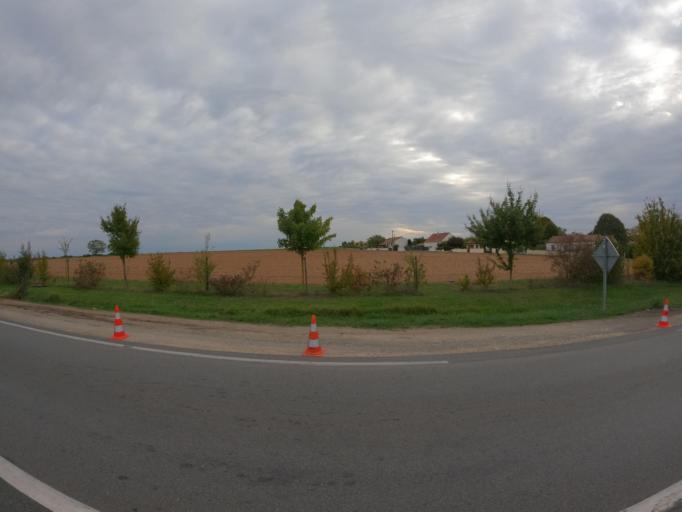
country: FR
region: Poitou-Charentes
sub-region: Departement de la Vienne
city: Vouille
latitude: 46.6442
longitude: 0.1837
